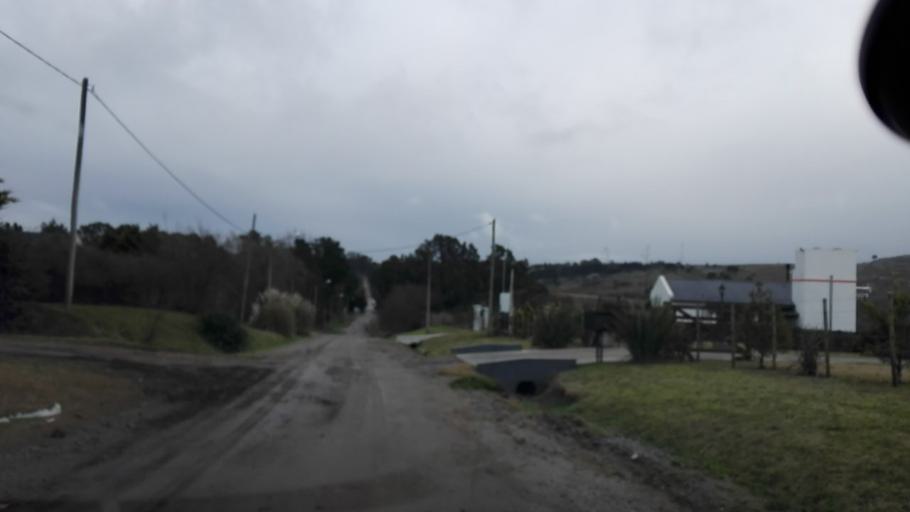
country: AR
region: Buenos Aires
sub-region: Partido de Tandil
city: Tandil
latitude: -37.3482
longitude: -59.1650
